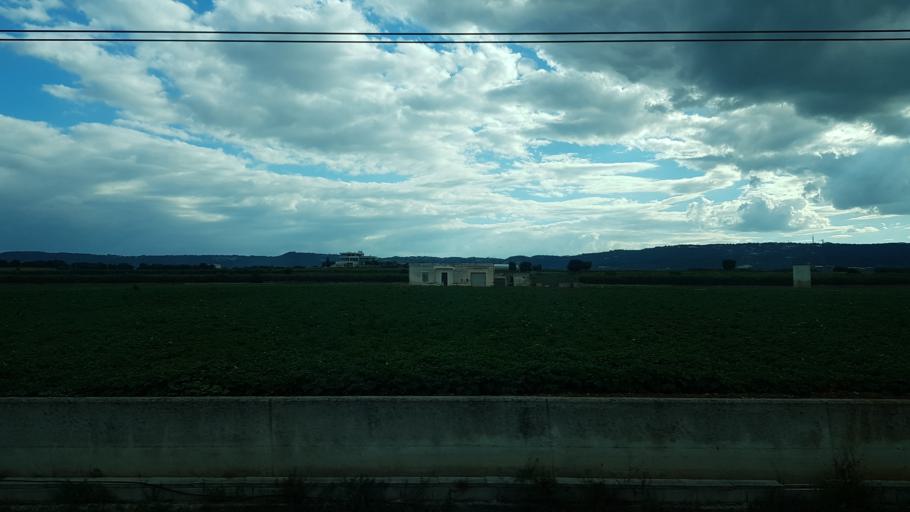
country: IT
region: Apulia
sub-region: Provincia di Brindisi
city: Fasano
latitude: 40.8471
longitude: 17.3926
